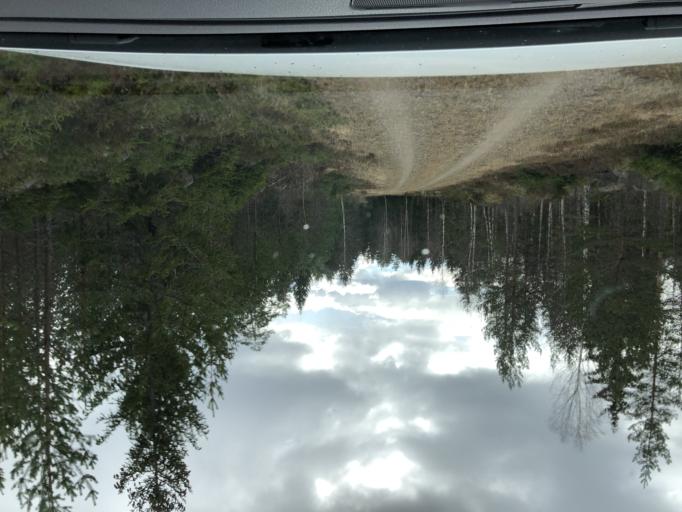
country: SE
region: Gaevleborg
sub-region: Gavle Kommun
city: Hedesunda
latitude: 60.3401
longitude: 17.0648
